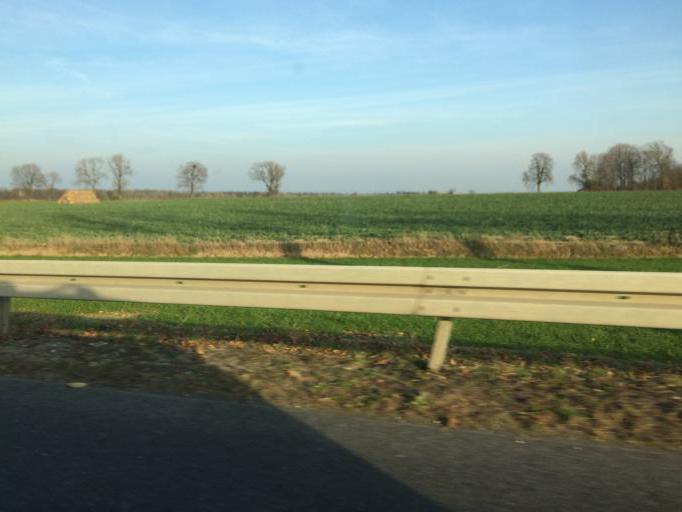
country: PL
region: Opole Voivodeship
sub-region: Powiat strzelecki
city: Strzelce Opolskie
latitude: 50.4960
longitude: 18.3371
